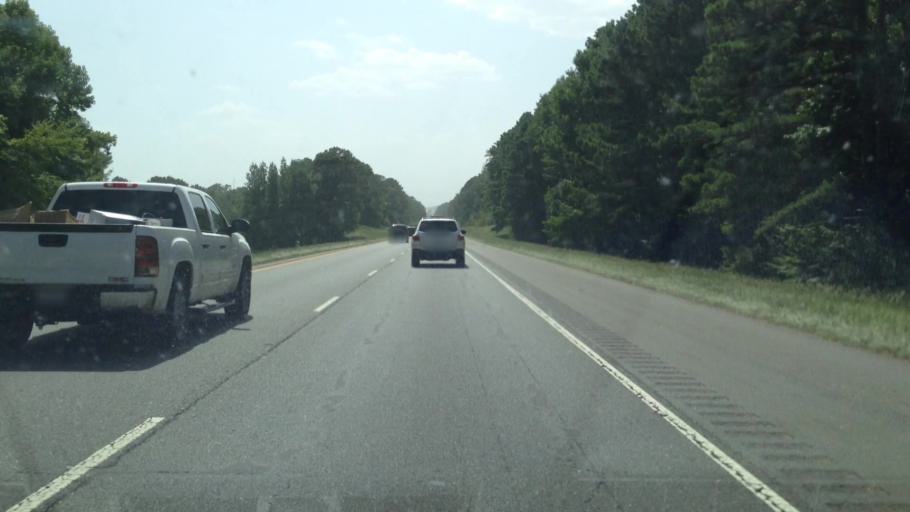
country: US
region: Louisiana
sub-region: Bossier Parish
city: Eastwood
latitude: 32.5423
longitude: -93.5520
